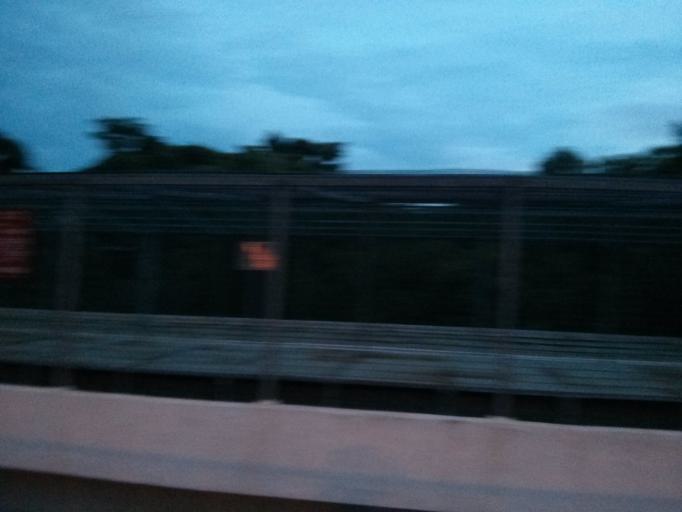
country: SG
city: Singapore
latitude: 1.3231
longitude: 103.7601
